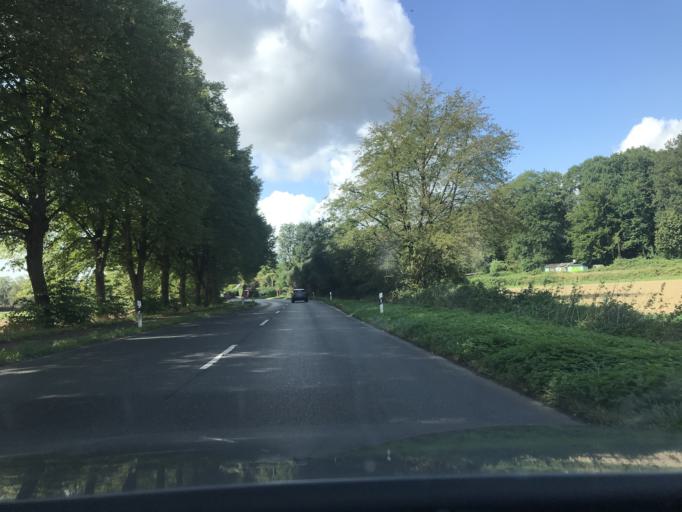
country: DE
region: North Rhine-Westphalia
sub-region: Regierungsbezirk Dusseldorf
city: Erkrath
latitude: 51.2259
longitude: 6.8778
